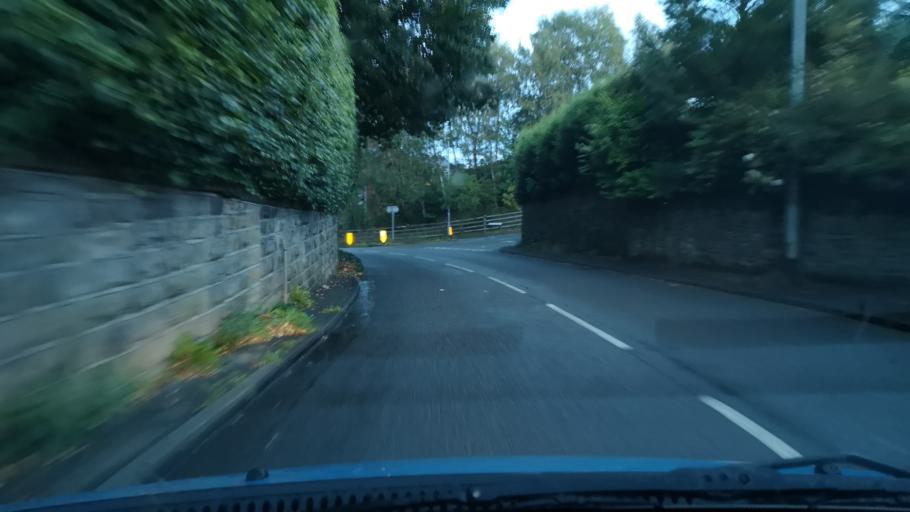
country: GB
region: England
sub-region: Kirklees
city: Batley
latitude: 53.7227
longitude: -1.6310
